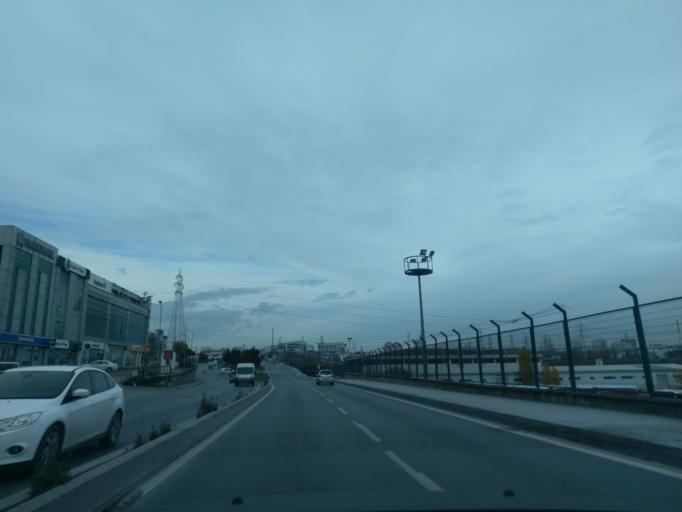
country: TR
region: Istanbul
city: Basaksehir
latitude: 41.0604
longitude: 28.7898
